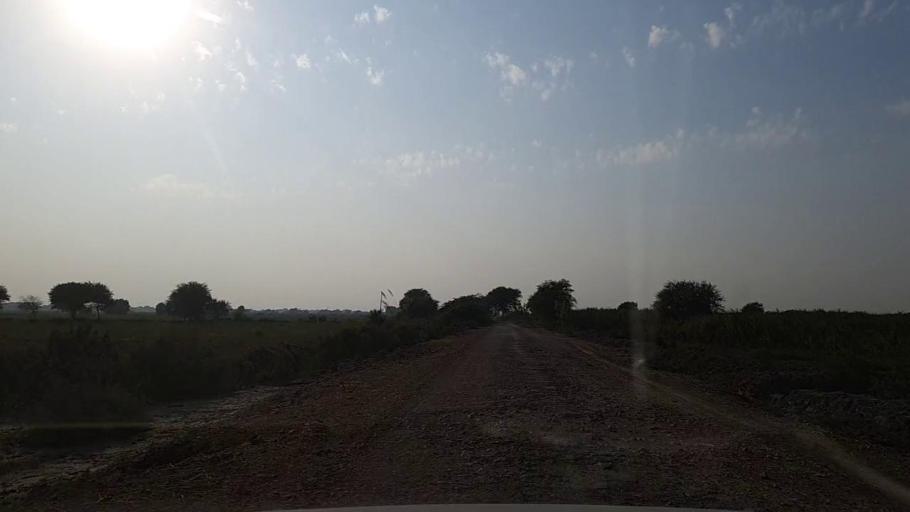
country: PK
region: Sindh
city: Mirpur Batoro
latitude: 24.7898
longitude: 68.2579
